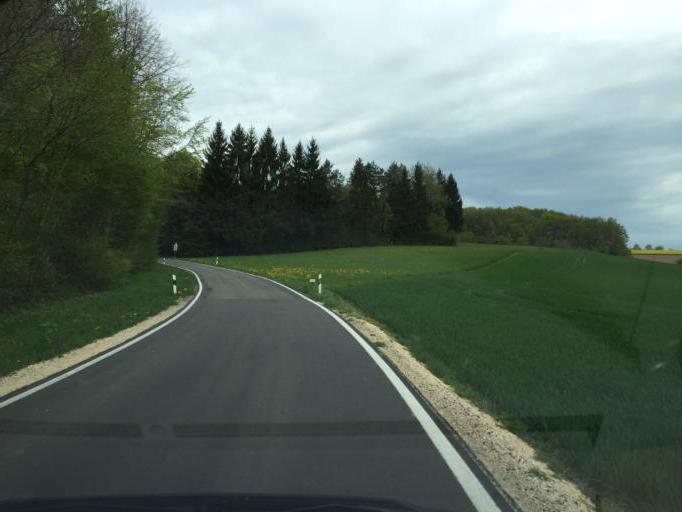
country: DE
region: Baden-Wuerttemberg
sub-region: Freiburg Region
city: Busingen
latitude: 47.7054
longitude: 8.6826
